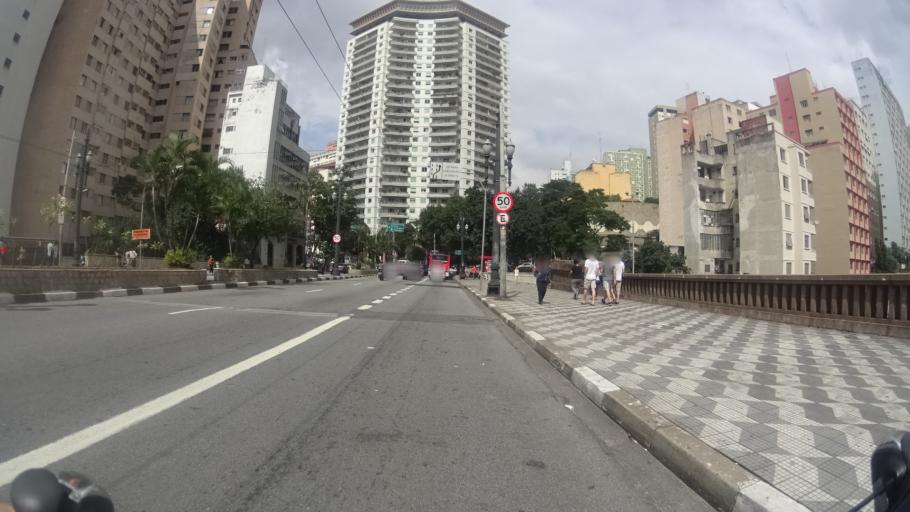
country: BR
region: Sao Paulo
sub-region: Sao Paulo
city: Sao Paulo
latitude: -23.5494
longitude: -46.6424
